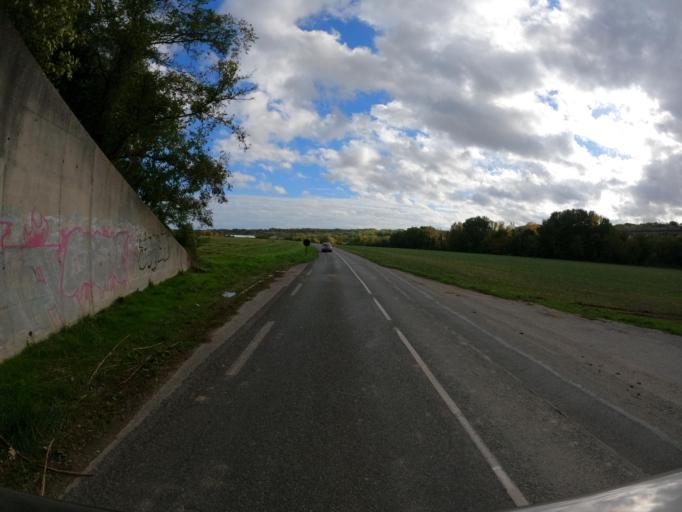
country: FR
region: Ile-de-France
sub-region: Departement de Seine-et-Marne
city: Chalifert
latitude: 48.9013
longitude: 2.7807
